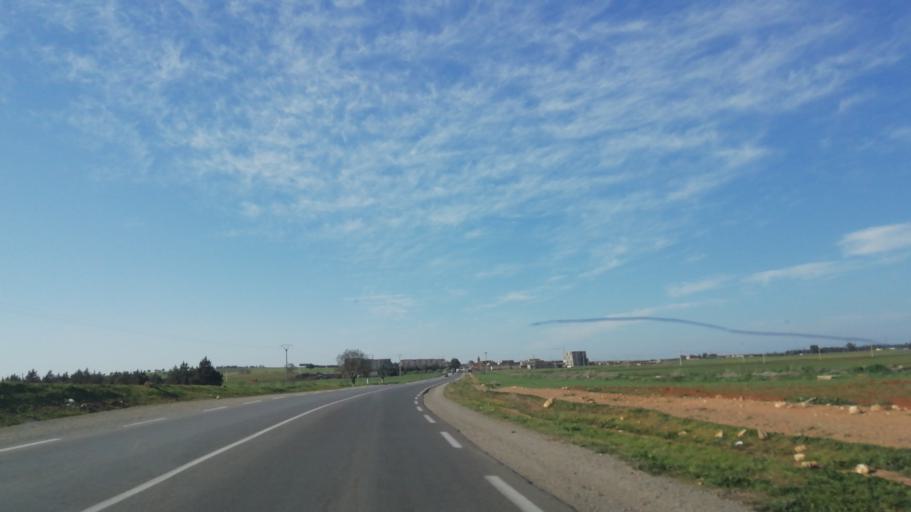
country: DZ
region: Tlemcen
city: Ouled Mimoun
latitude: 35.0294
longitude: -0.8706
